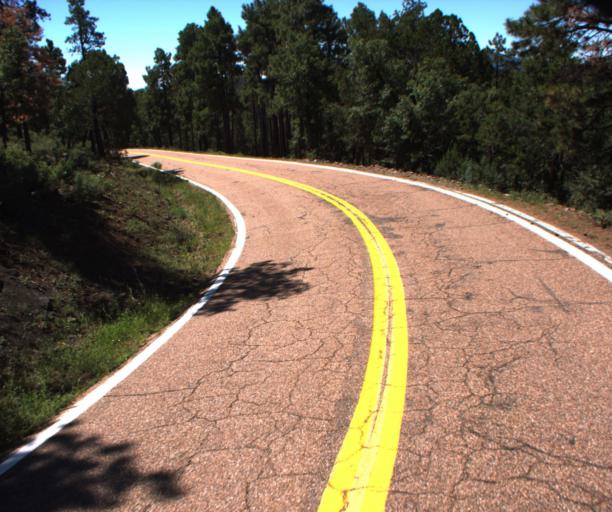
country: US
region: Arizona
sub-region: Greenlee County
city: Morenci
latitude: 33.5263
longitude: -109.3084
